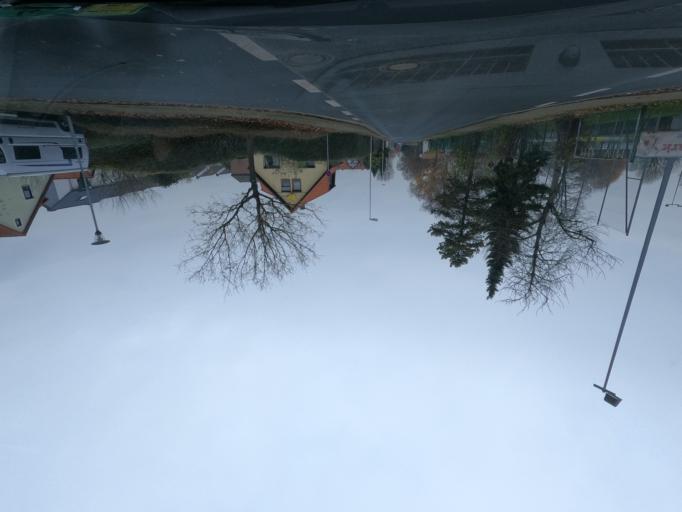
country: DE
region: Lower Saxony
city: Wolfenbuettel
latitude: 52.1928
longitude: 10.5882
